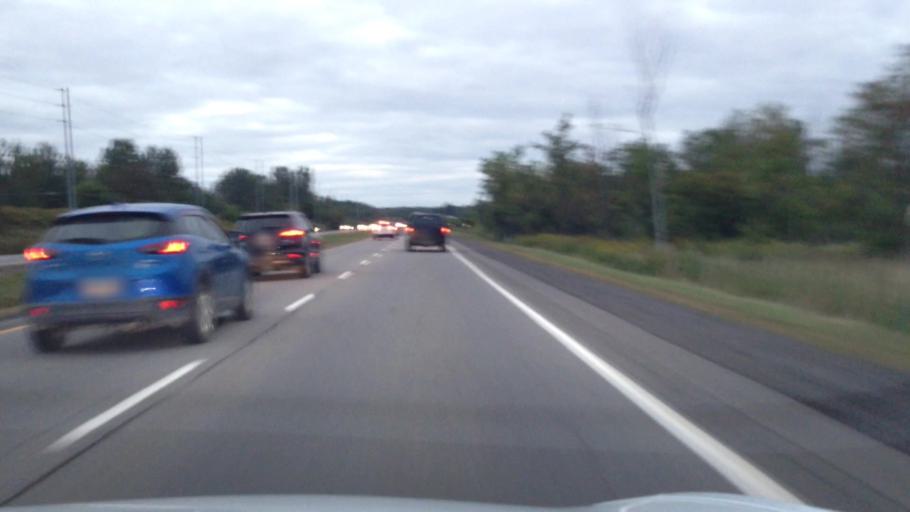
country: CA
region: Ontario
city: Ottawa
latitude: 45.4298
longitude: -75.5560
